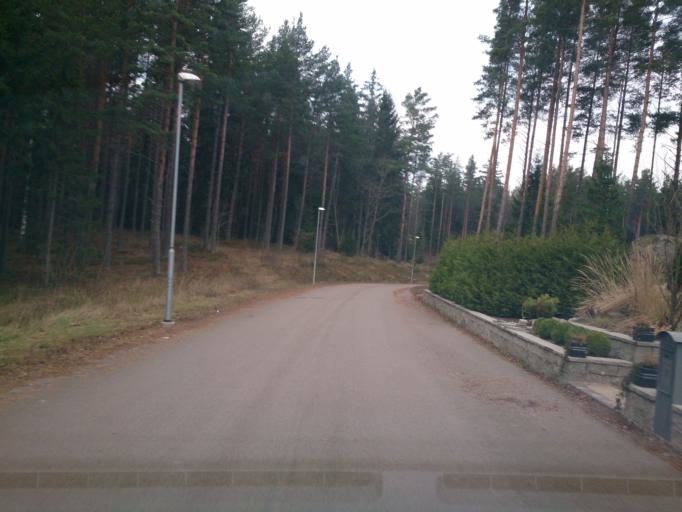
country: SE
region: OEstergoetland
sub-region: Linkopings Kommun
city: Sturefors
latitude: 58.3110
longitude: 15.8702
